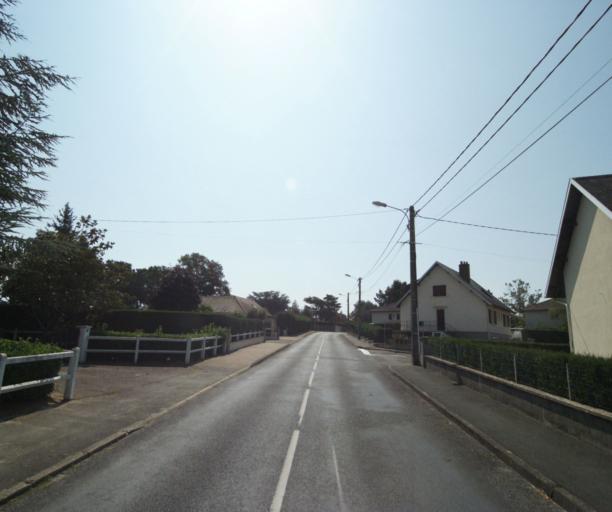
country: FR
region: Bourgogne
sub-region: Departement de Saone-et-Loire
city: Gueugnon
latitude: 46.5985
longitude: 4.0761
